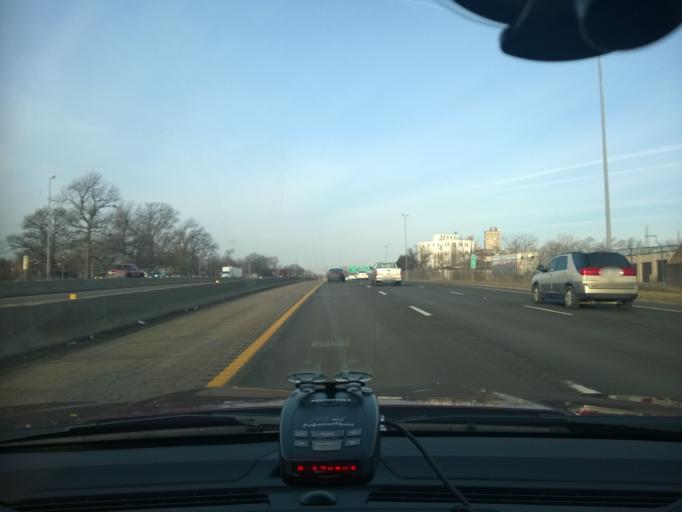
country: US
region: Missouri
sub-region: Saint Louis County
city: Pine Lawn
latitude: 38.6830
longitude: -90.2340
